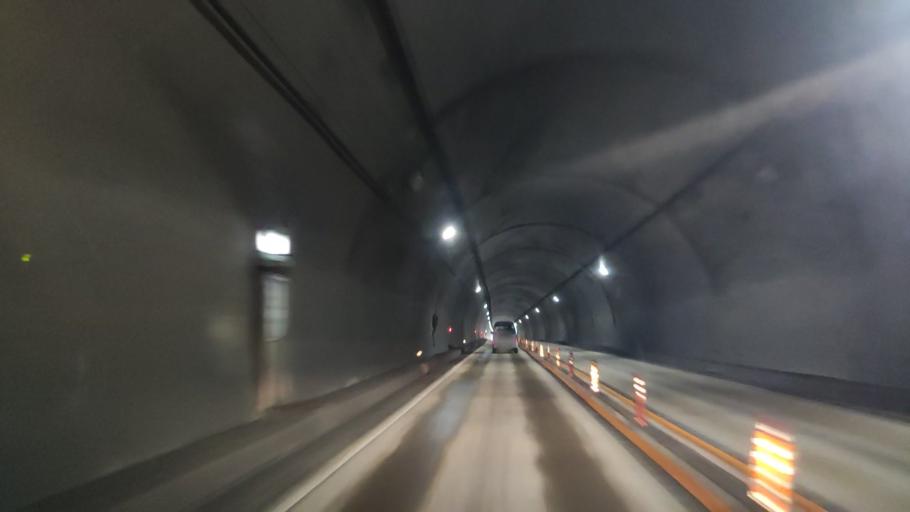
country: JP
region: Tokushima
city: Kamojimacho-jogejima
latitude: 34.1124
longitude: 134.3210
